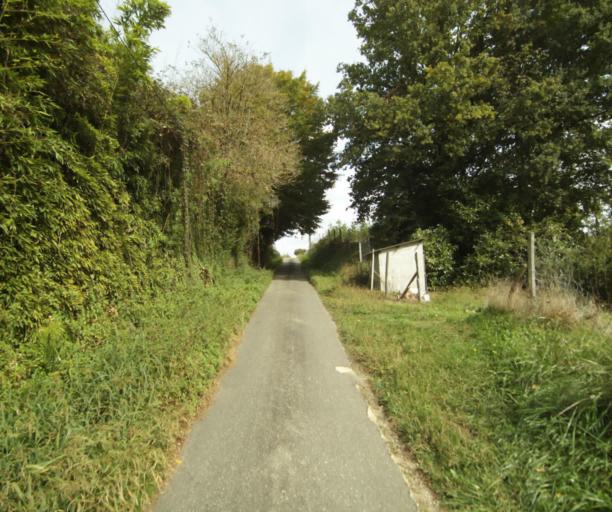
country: FR
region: Midi-Pyrenees
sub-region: Departement du Gers
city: Eauze
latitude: 43.8443
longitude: 0.1049
